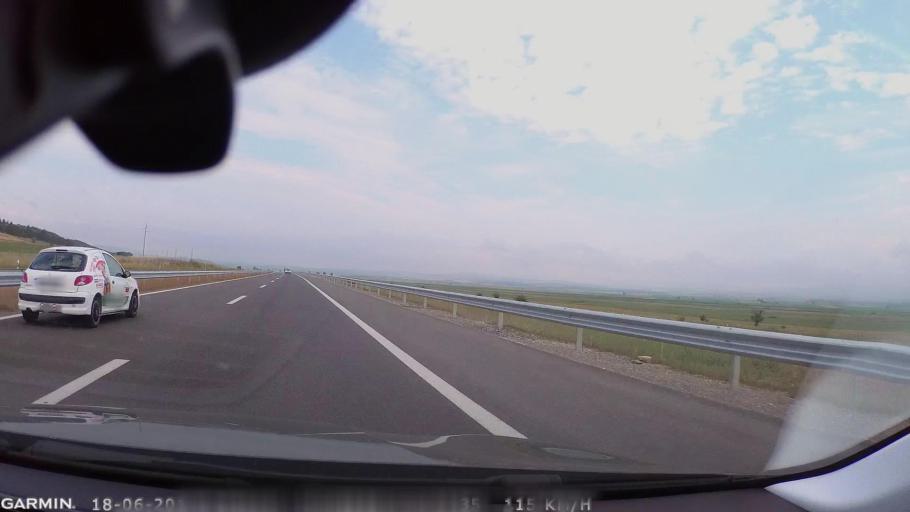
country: MK
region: Sveti Nikole
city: Sveti Nikole
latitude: 41.8037
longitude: 22.0717
